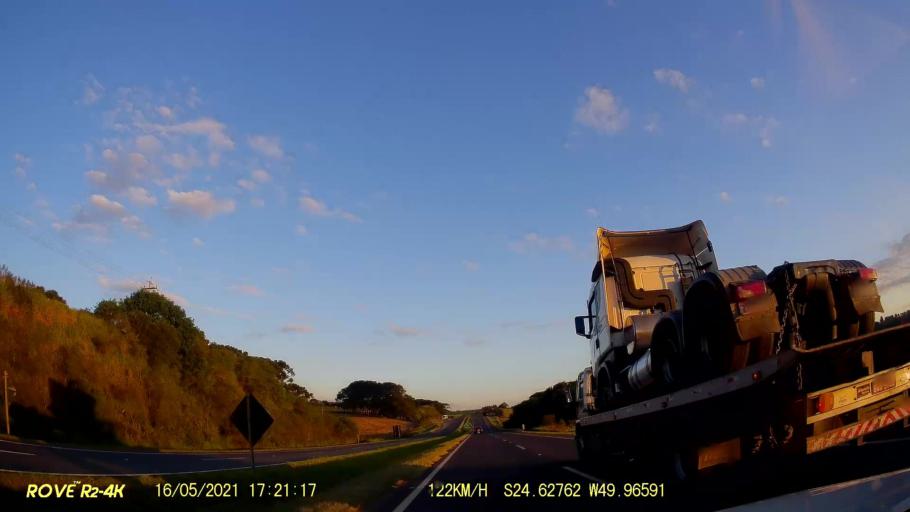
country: BR
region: Parana
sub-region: Pirai Do Sul
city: Pirai do Sul
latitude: -24.6281
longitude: -49.9659
